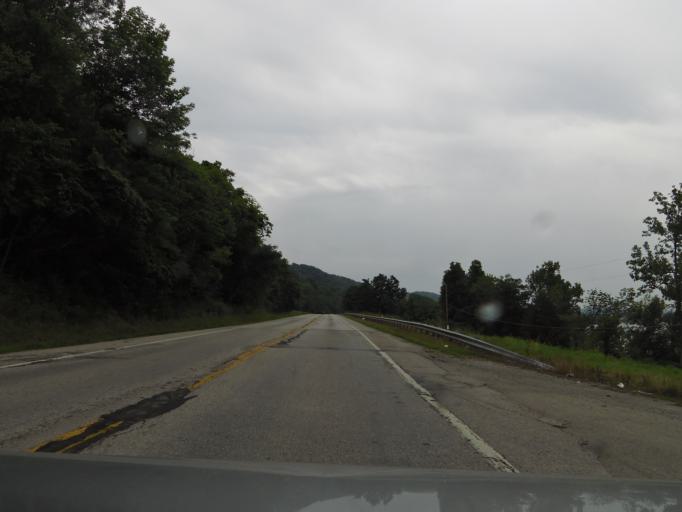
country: US
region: Ohio
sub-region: Brown County
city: Aberdeen
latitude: 38.7026
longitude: -83.7900
